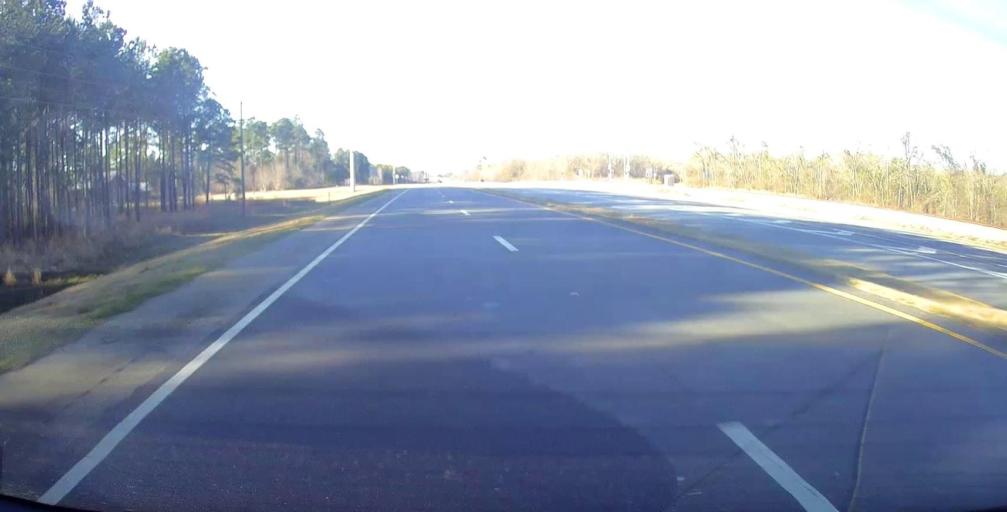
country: US
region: Georgia
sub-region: Lee County
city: Leesburg
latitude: 31.8739
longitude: -84.2396
